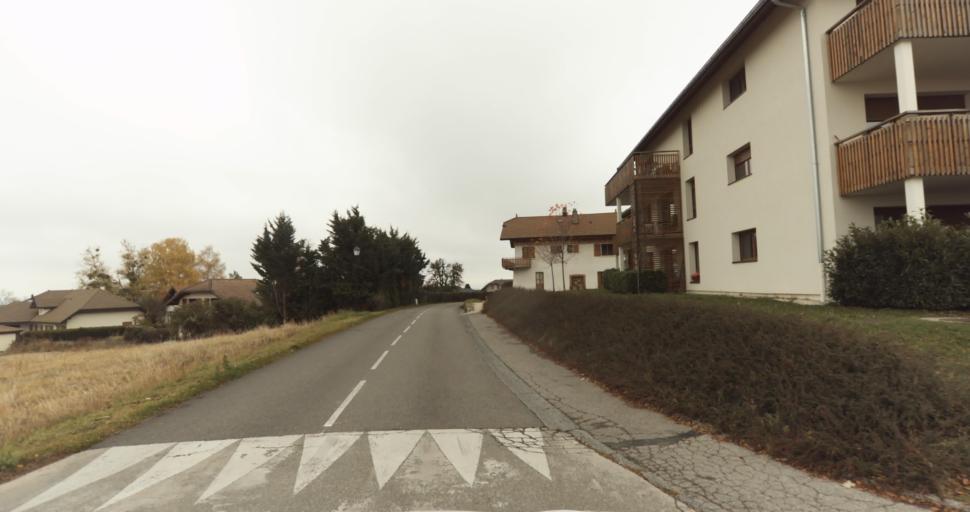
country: FR
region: Rhone-Alpes
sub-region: Departement de la Haute-Savoie
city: Viuz-la-Chiesaz
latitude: 45.8408
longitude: 6.0840
